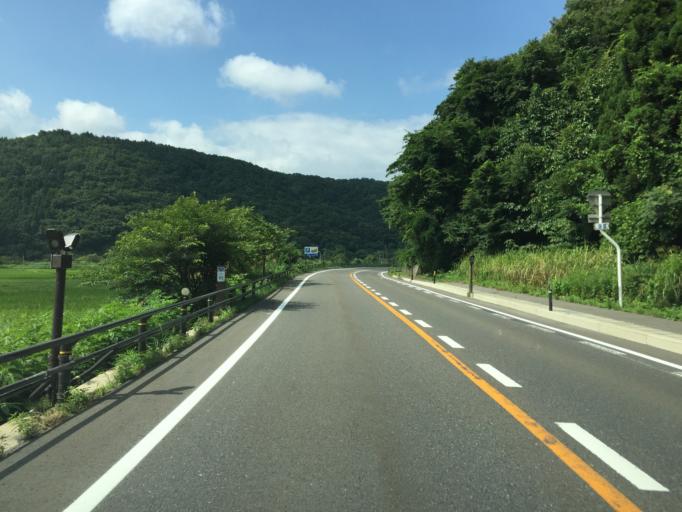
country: JP
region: Fukushima
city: Inawashiro
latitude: 37.4846
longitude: 140.1835
